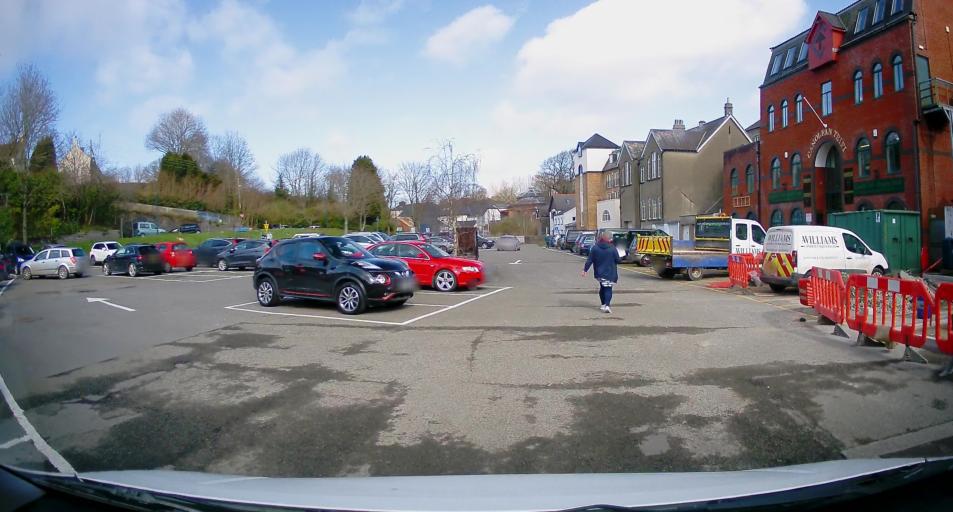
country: GB
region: Wales
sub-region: County of Ceredigion
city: Cardigan
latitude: 52.0840
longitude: -4.6616
